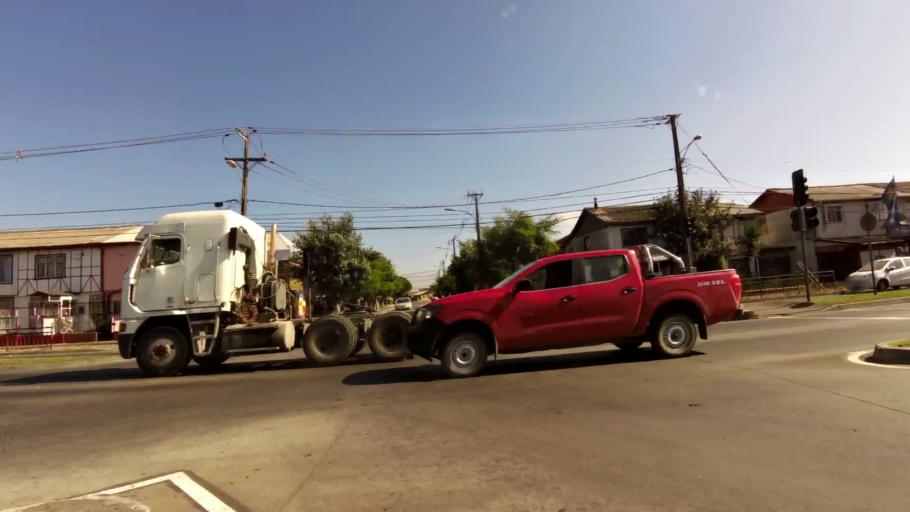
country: CL
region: Biobio
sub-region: Provincia de Concepcion
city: Talcahuano
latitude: -36.7803
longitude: -73.0962
